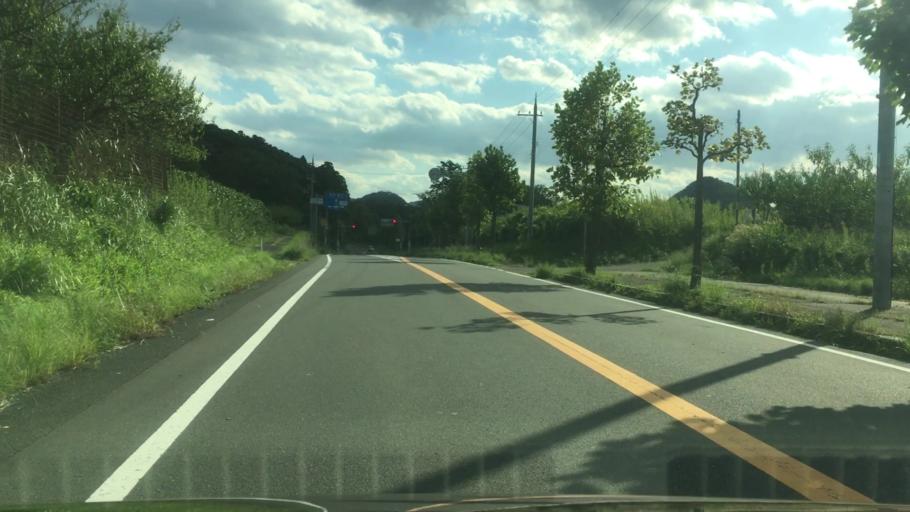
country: JP
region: Hyogo
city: Toyooka
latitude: 35.6283
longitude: 134.9300
